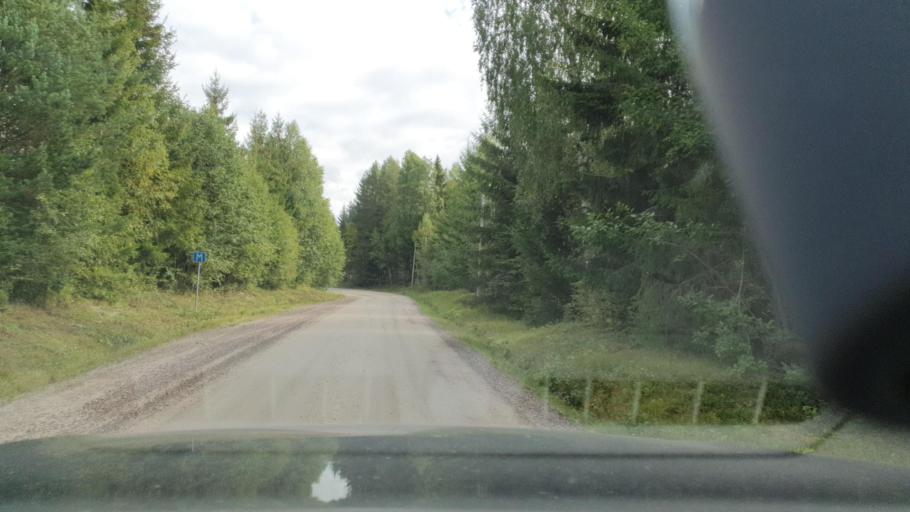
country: SE
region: Vaermland
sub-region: Hagfors Kommun
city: Ekshaerad
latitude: 60.1979
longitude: 13.5324
